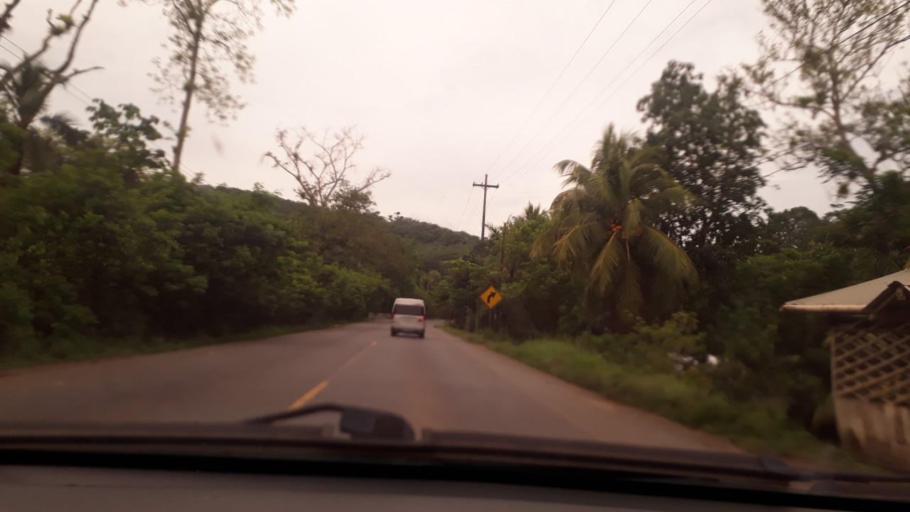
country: GT
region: Izabal
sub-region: Municipio de Puerto Barrios
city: Puerto Barrios
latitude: 15.6168
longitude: -88.5671
